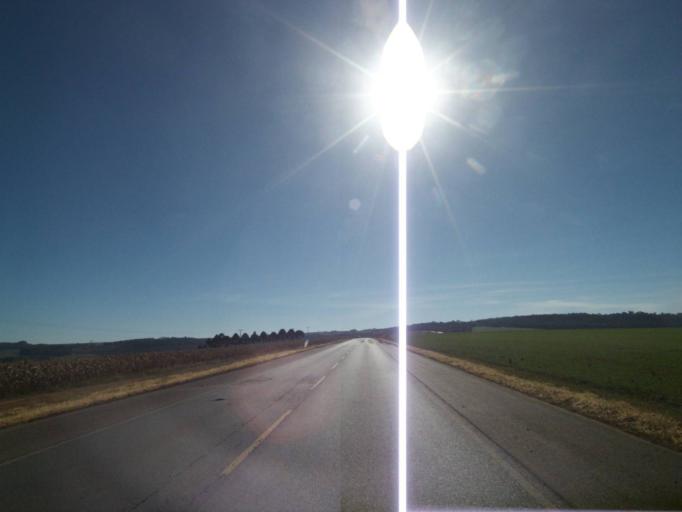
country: BR
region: Parana
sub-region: Tibagi
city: Tibagi
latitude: -24.3878
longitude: -50.3345
